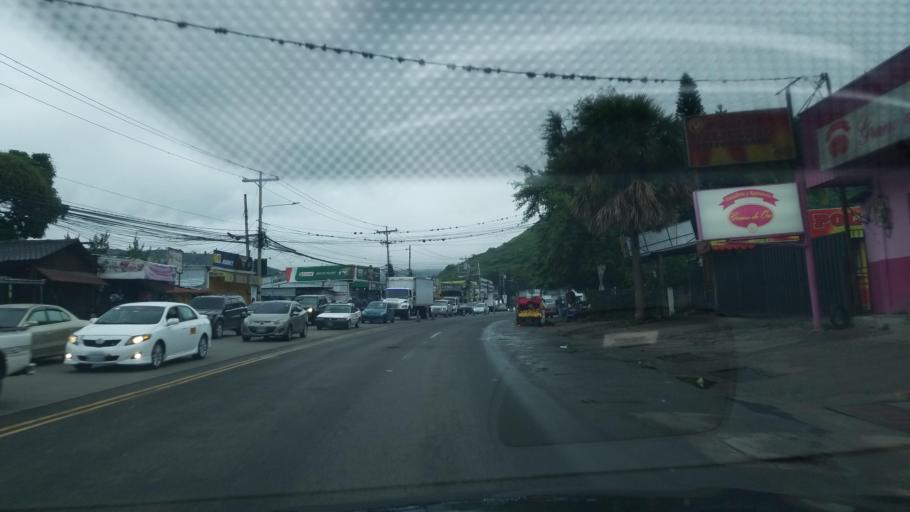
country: HN
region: Francisco Morazan
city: Yaguacire
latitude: 14.0442
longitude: -87.2113
